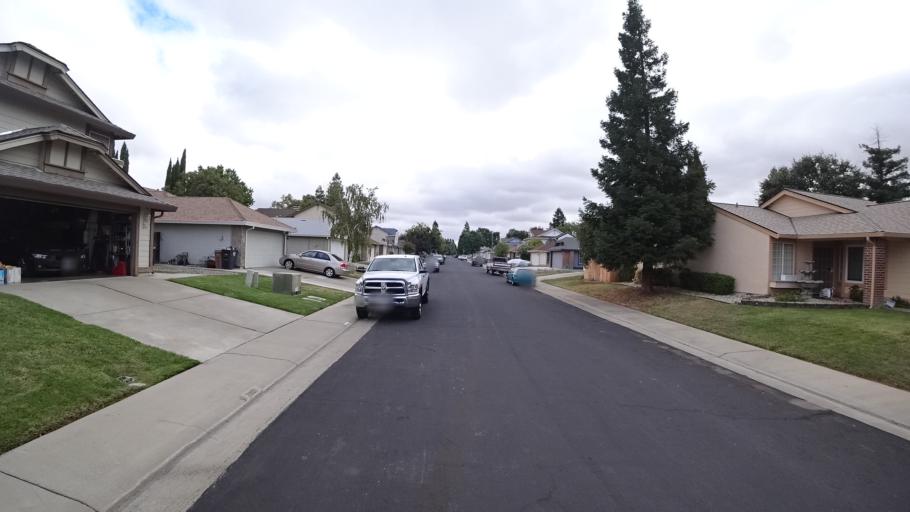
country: US
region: California
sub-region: Sacramento County
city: Laguna
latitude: 38.4140
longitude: -121.4218
